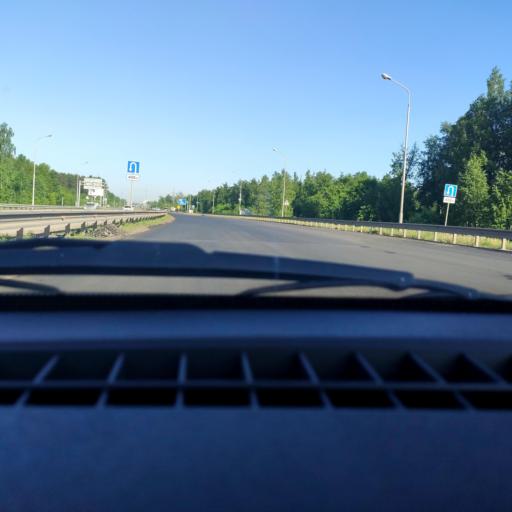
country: RU
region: Bashkortostan
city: Ufa
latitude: 54.6642
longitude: 56.0731
